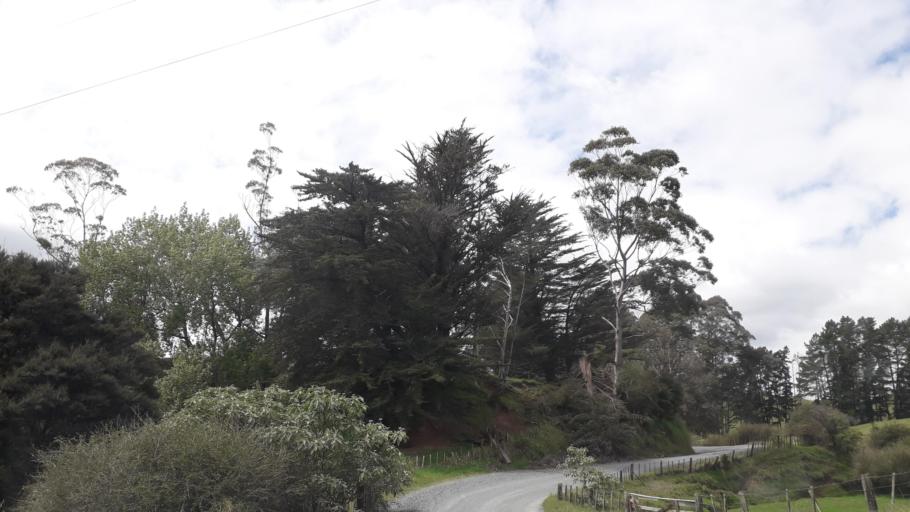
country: NZ
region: Northland
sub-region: Far North District
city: Taipa
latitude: -35.0933
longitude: 173.5204
